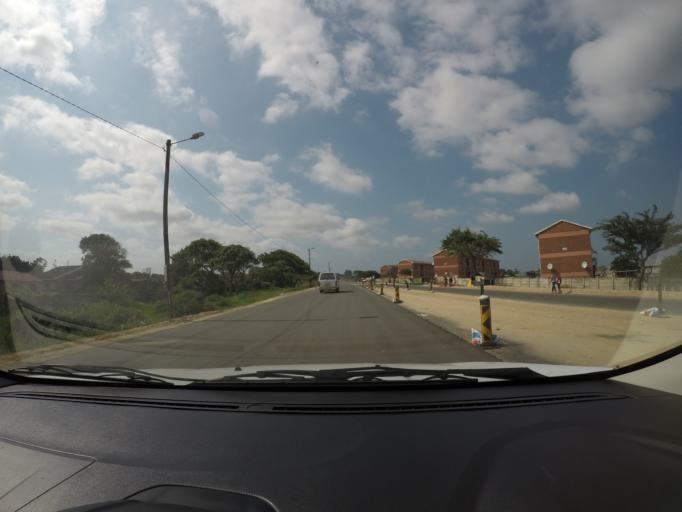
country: ZA
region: KwaZulu-Natal
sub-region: uThungulu District Municipality
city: eSikhawini
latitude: -28.8734
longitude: 31.9014
